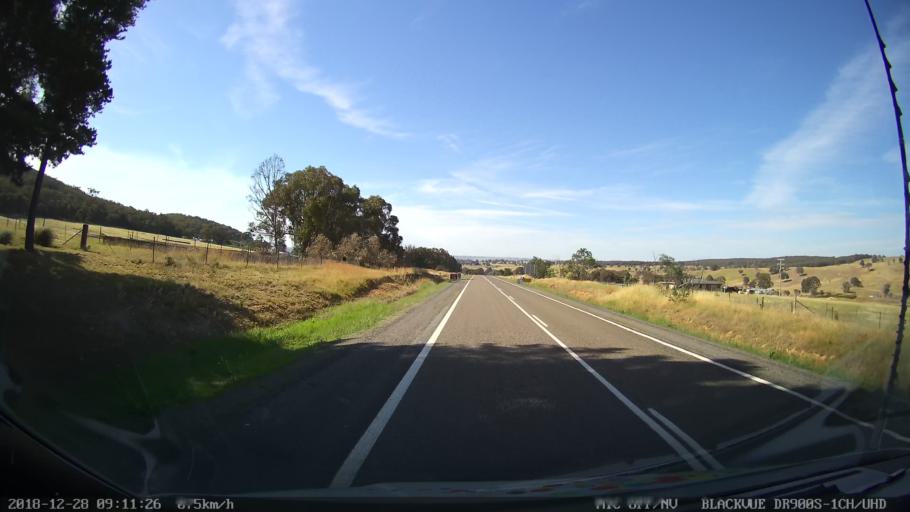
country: AU
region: New South Wales
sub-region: Upper Lachlan Shire
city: Crookwell
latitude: -34.2434
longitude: 149.3384
